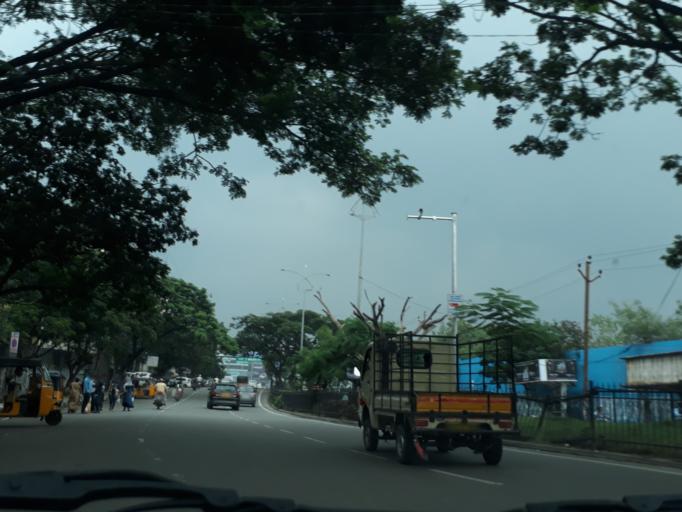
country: IN
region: Telangana
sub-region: Rangareddi
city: Kukatpalli
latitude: 17.4267
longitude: 78.4163
